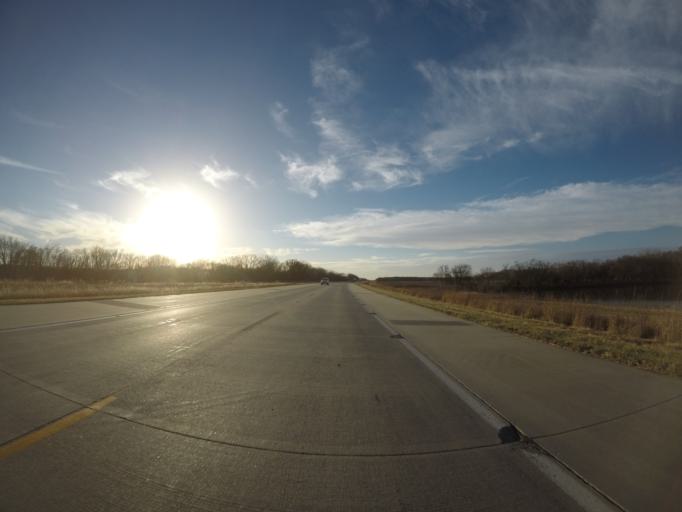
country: US
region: Kansas
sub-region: Lyon County
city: Emporia
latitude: 38.4067
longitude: -96.3073
